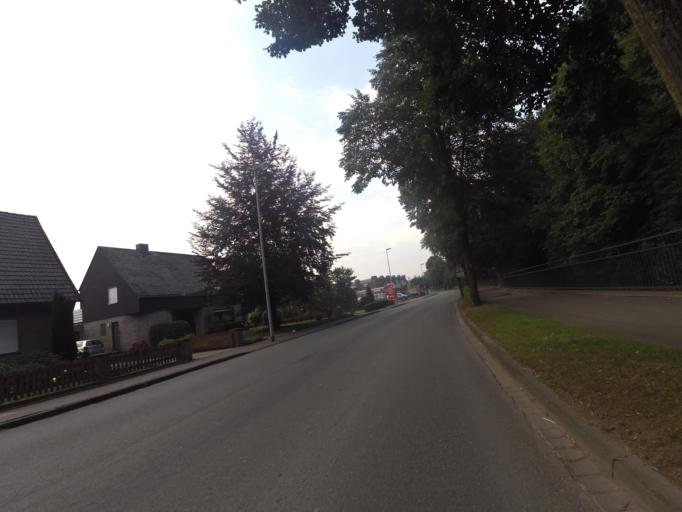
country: DE
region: North Rhine-Westphalia
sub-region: Regierungsbezirk Munster
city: Isselburg
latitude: 51.8443
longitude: 6.4235
